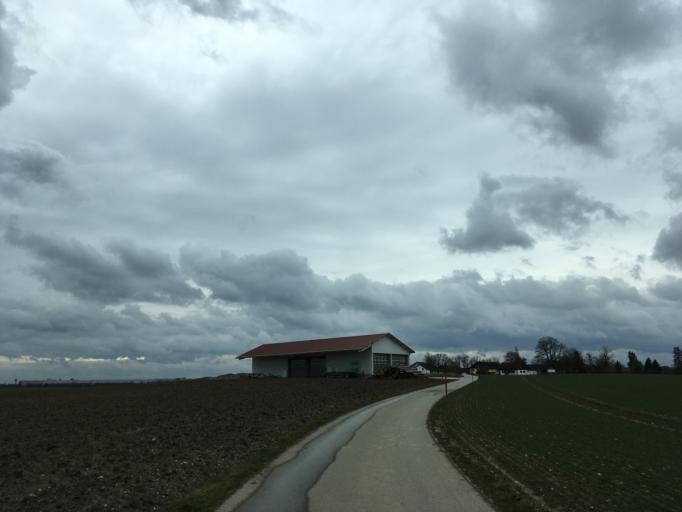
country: DE
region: Bavaria
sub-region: Upper Bavaria
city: Anzing
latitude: 48.1718
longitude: 11.8531
